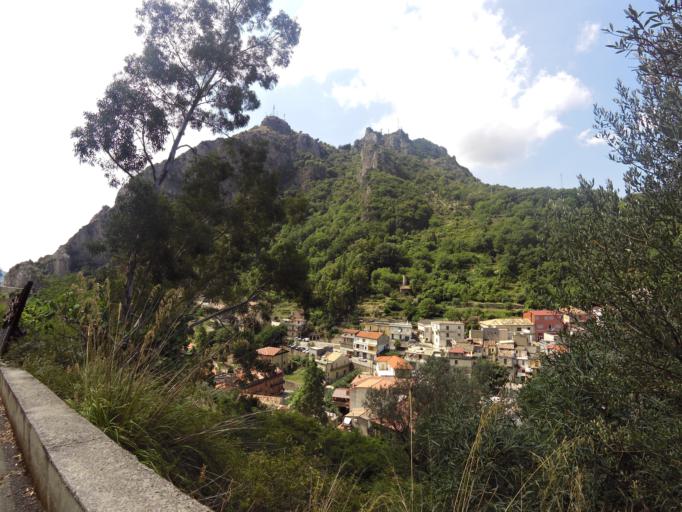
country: IT
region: Calabria
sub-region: Provincia di Reggio Calabria
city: Pazzano
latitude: 38.4760
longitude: 16.4538
